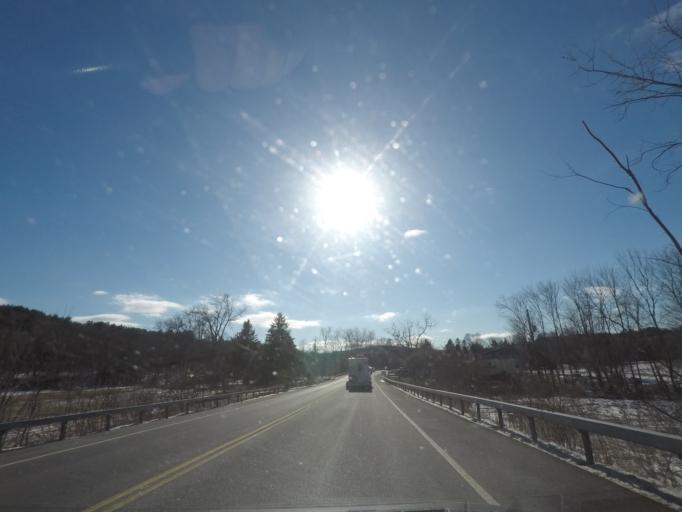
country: US
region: New York
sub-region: Columbia County
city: Chatham
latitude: 42.4163
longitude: -73.5134
